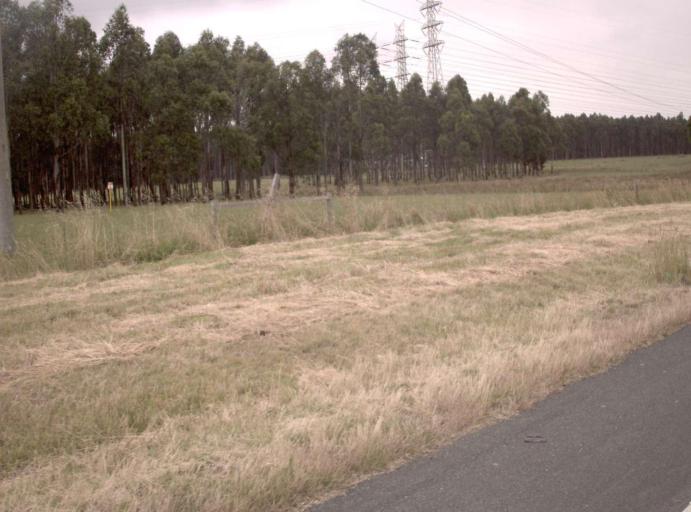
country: AU
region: Victoria
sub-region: Latrobe
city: Morwell
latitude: -38.2776
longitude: 146.4184
